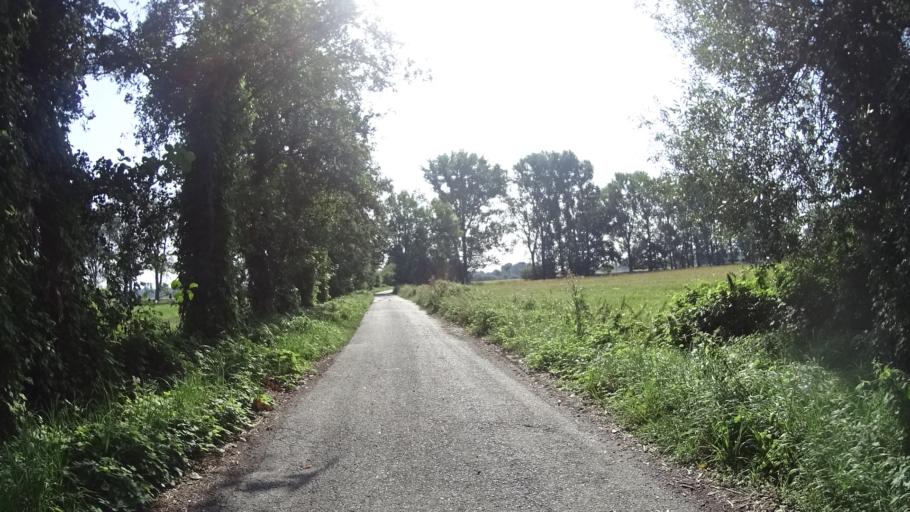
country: DE
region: Brandenburg
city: Neu Zauche
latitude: 51.9030
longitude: 14.0843
